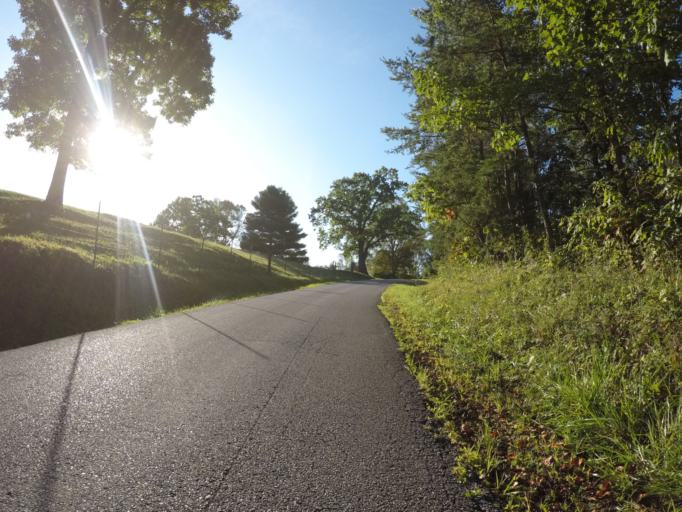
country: US
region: Ohio
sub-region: Lawrence County
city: Coal Grove
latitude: 38.5977
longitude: -82.5475
